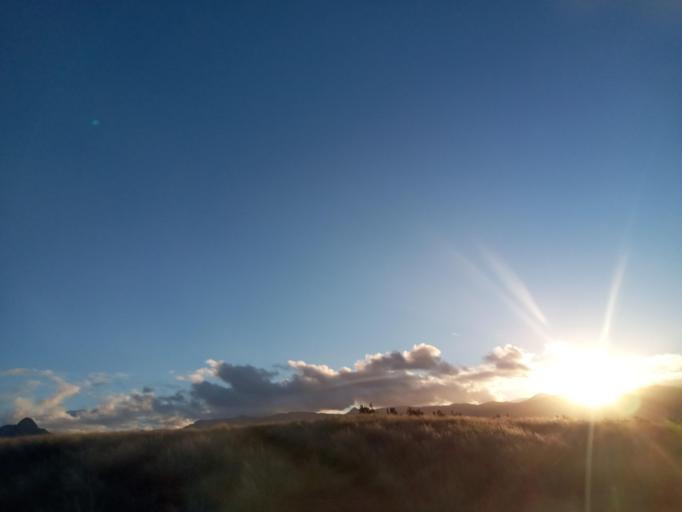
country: MG
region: Anosy
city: Fort Dauphin
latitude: -24.5152
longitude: 47.2457
